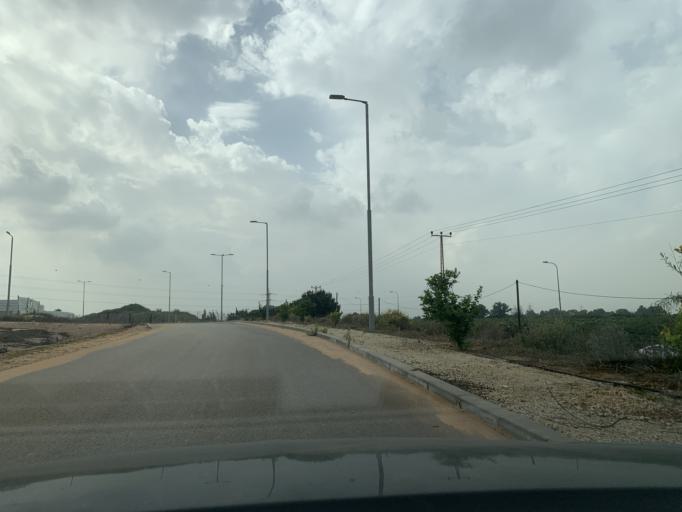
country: IL
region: Central District
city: Tirah
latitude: 32.2173
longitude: 34.9336
